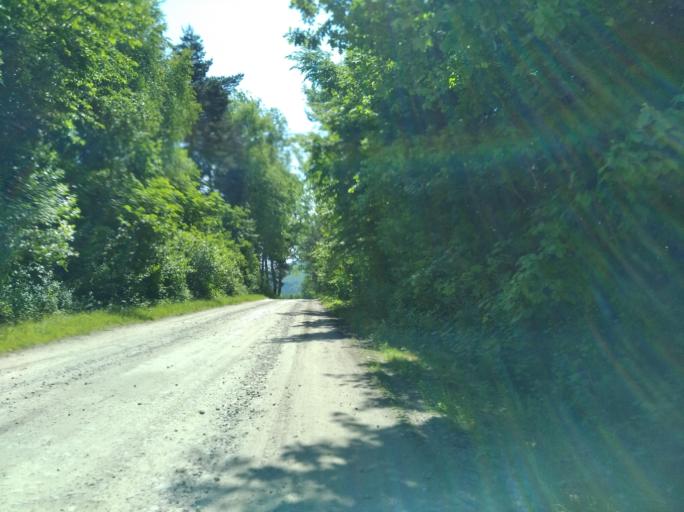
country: PL
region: Subcarpathian Voivodeship
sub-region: Powiat krosnienski
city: Odrzykon
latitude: 49.7678
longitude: 21.7791
